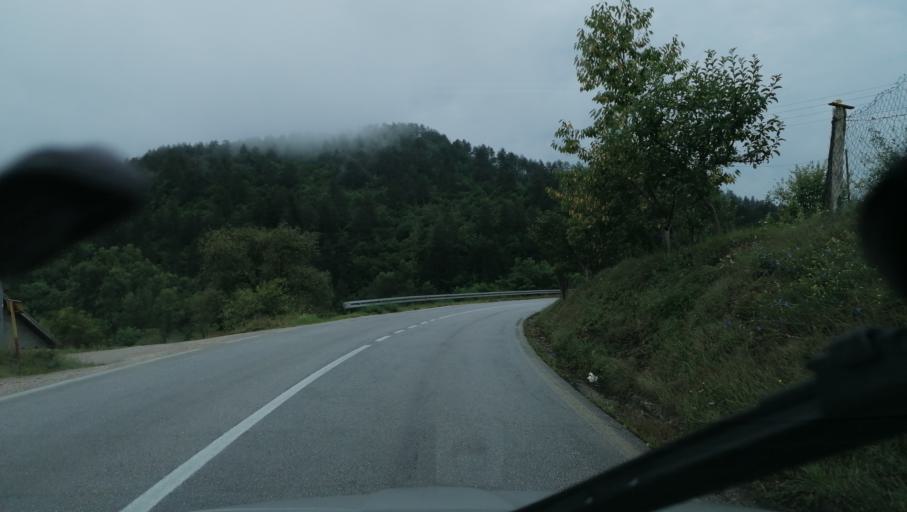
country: BA
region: Republika Srpska
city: Visegrad
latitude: 43.7848
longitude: 19.3246
